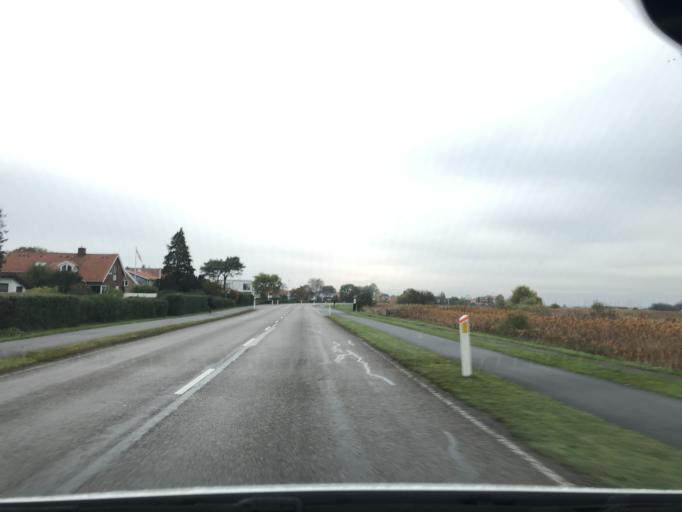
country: DK
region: Capital Region
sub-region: Dragor Kommune
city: Dragor
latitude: 55.5867
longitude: 12.6647
